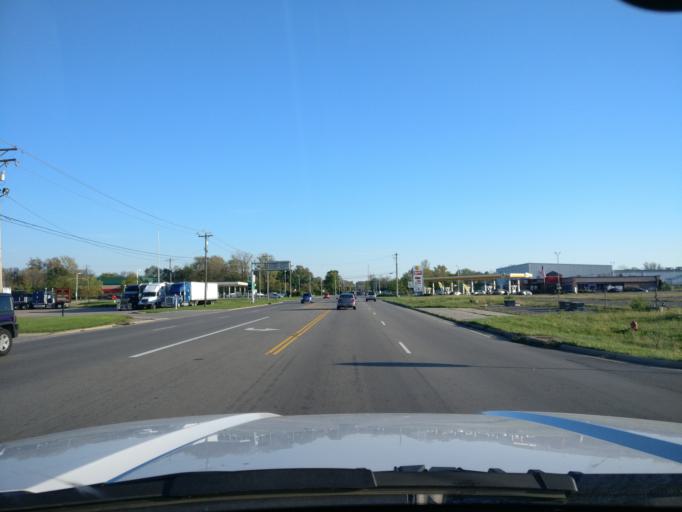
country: US
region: Ohio
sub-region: Warren County
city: Franklin
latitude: 39.5415
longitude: -84.2917
